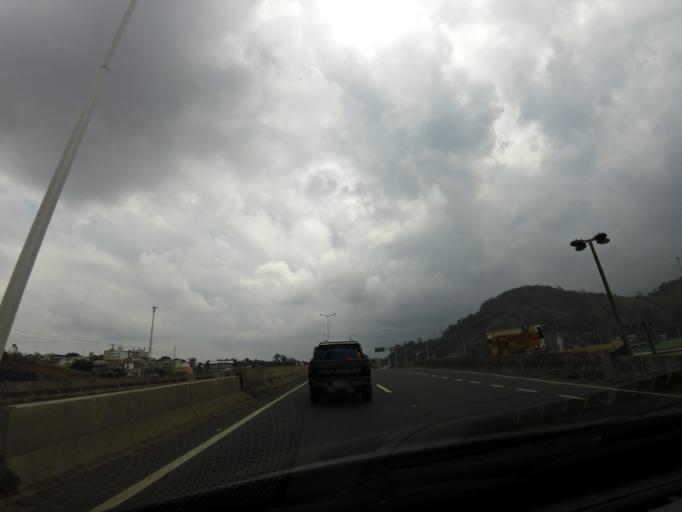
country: BR
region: Espirito Santo
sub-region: Vitoria
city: Vitoria
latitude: -20.3427
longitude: -40.4025
